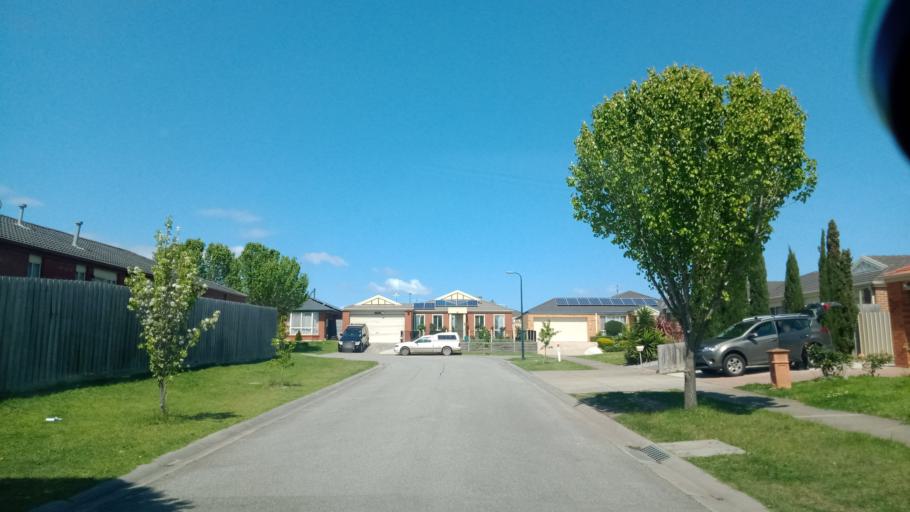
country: AU
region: Victoria
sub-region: Casey
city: Cranbourne West
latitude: -38.0939
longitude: 145.2594
